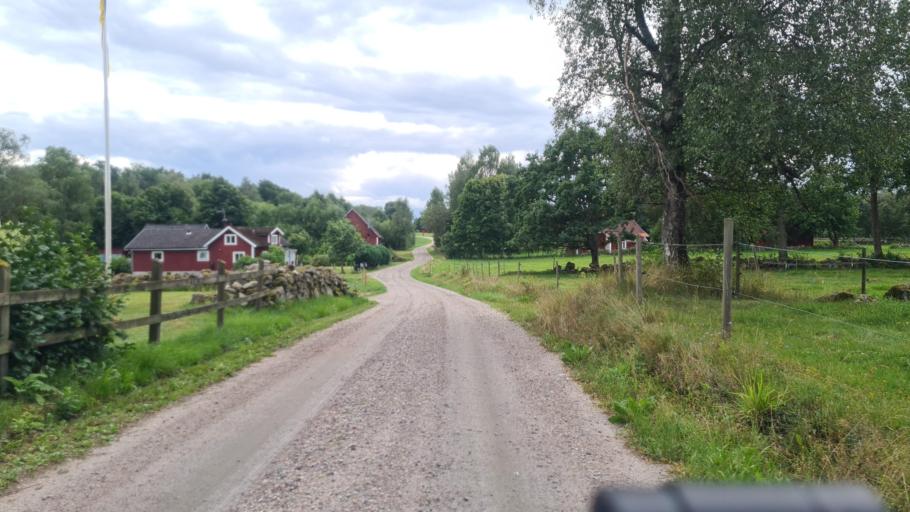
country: SE
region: Kronoberg
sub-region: Ljungby Kommun
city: Ljungby
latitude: 56.8159
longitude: 13.8512
